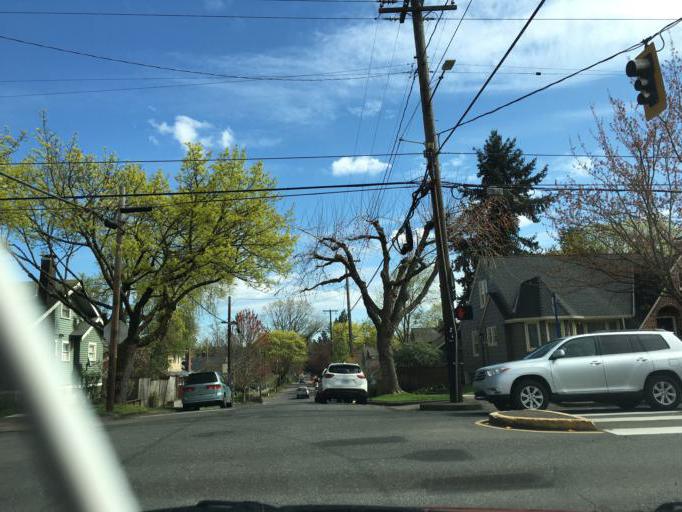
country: US
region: Oregon
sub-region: Clackamas County
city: Milwaukie
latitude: 45.4774
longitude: -122.6483
